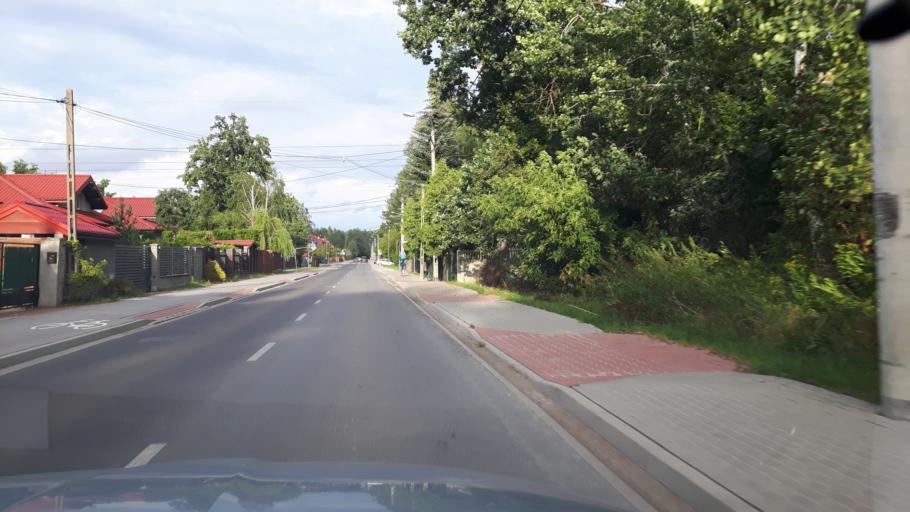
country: PL
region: Masovian Voivodeship
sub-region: Powiat wolominski
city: Marki
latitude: 52.3286
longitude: 21.1301
